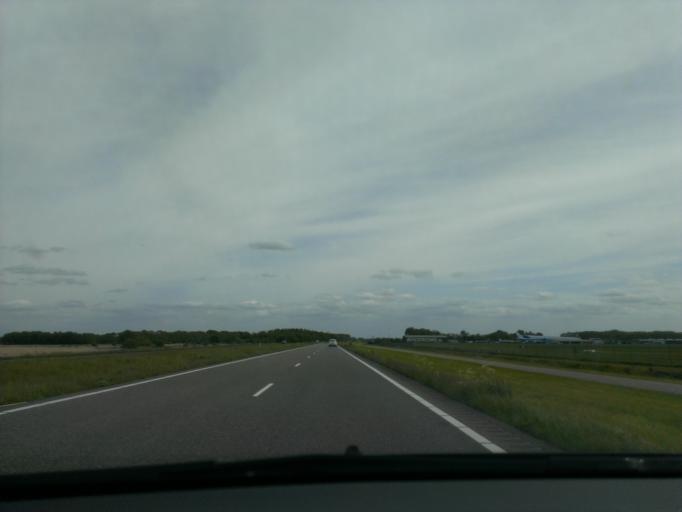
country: NL
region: Flevoland
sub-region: Gemeente Lelystad
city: Lelystad
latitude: 52.4664
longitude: 5.5238
